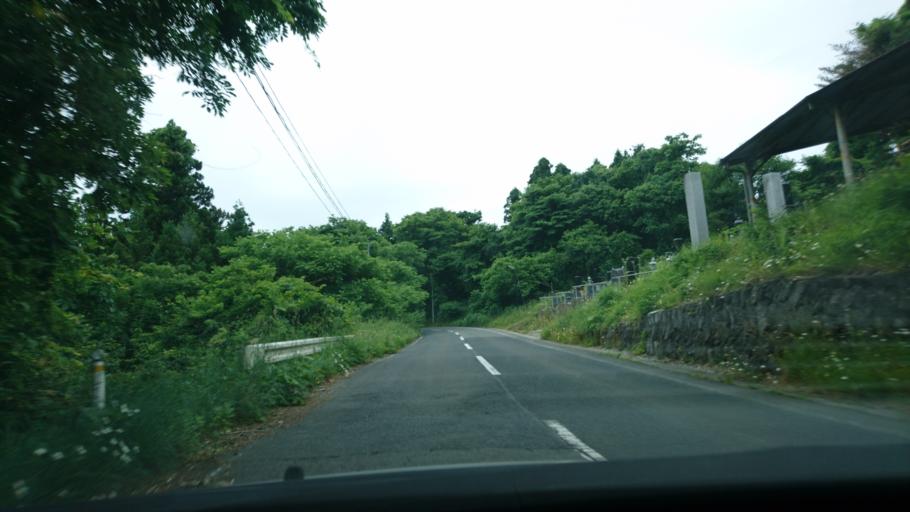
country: JP
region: Iwate
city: Ichinoseki
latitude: 38.9509
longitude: 141.2623
